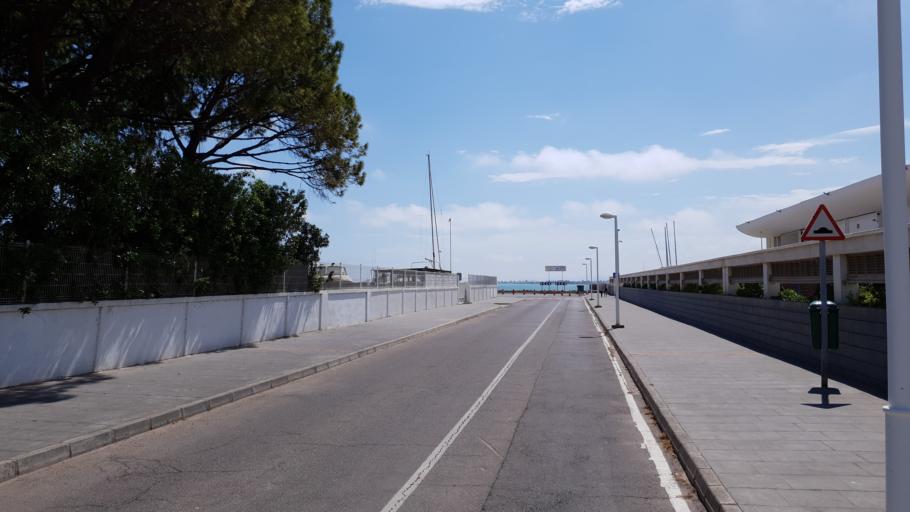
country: ES
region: Valencia
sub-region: Provincia de Castello
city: Burriana
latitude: 39.8628
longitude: -0.0751
